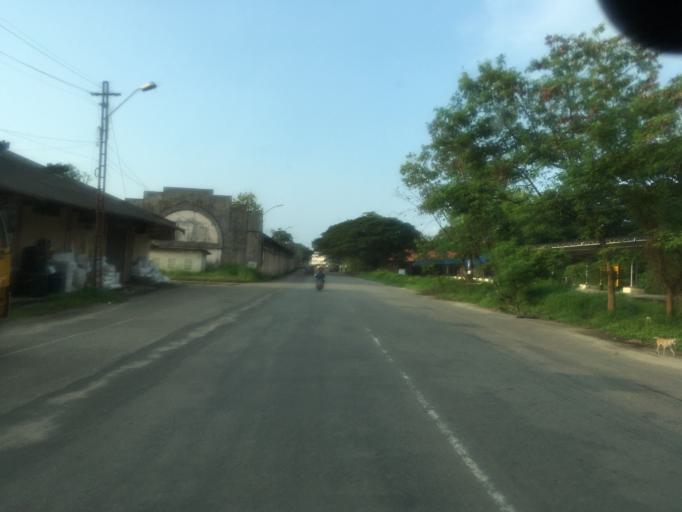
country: IN
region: Kerala
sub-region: Ernakulam
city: Cochin
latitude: 9.9586
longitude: 76.2677
